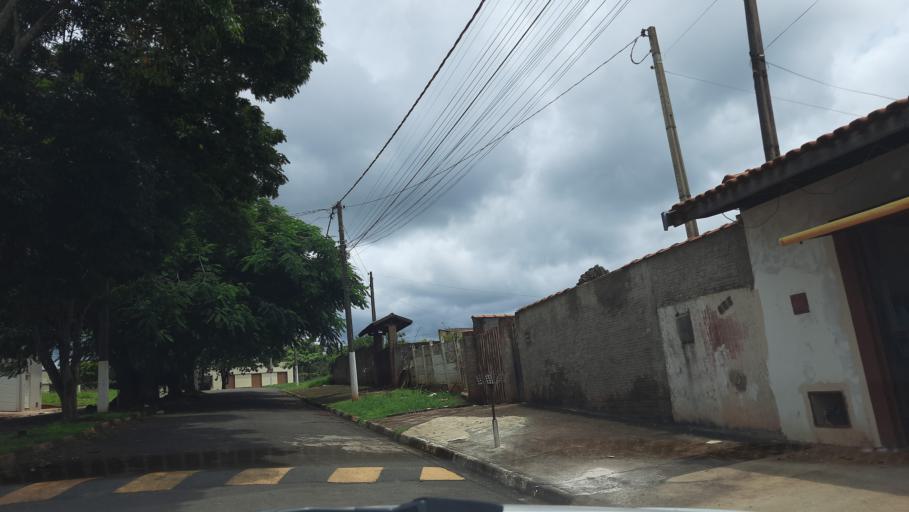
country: BR
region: Sao Paulo
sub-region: Casa Branca
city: Casa Branca
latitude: -21.7874
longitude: -47.0993
